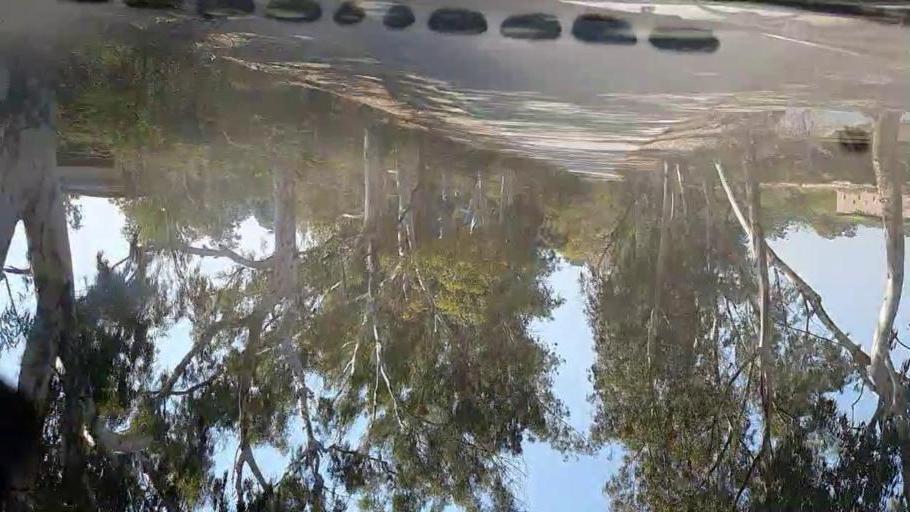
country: PK
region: Sindh
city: Mirpur Khas
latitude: 25.4718
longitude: 69.0260
